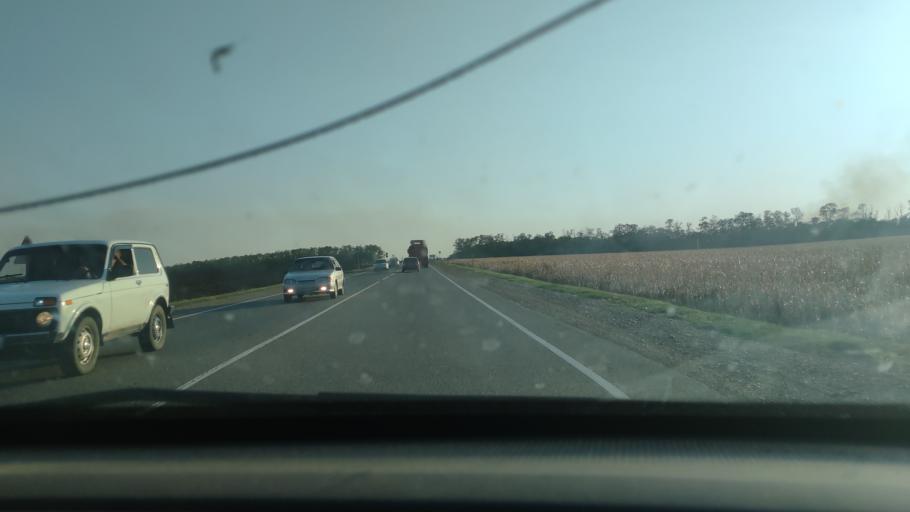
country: RU
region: Krasnodarskiy
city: Kanevskaya
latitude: 46.0429
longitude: 38.9875
